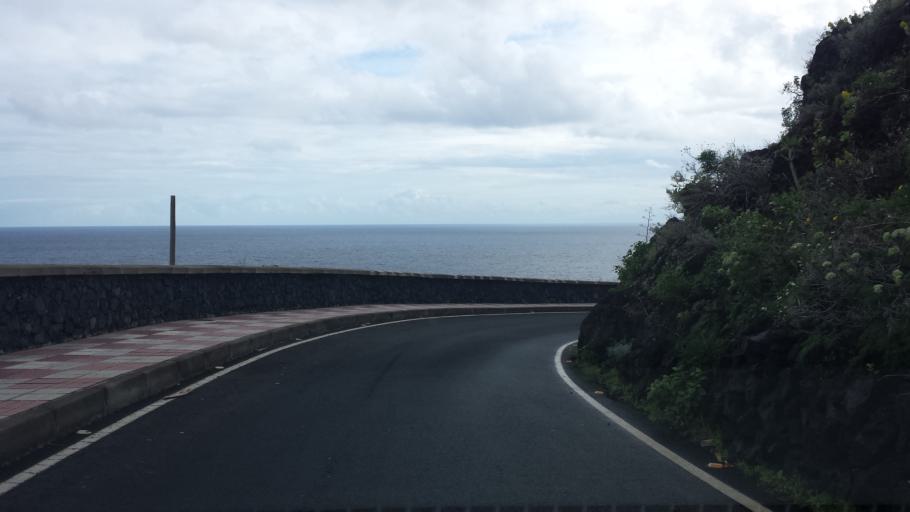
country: ES
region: Canary Islands
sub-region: Provincia de Santa Cruz de Tenerife
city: Brena Alta
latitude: 28.6570
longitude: -17.7640
